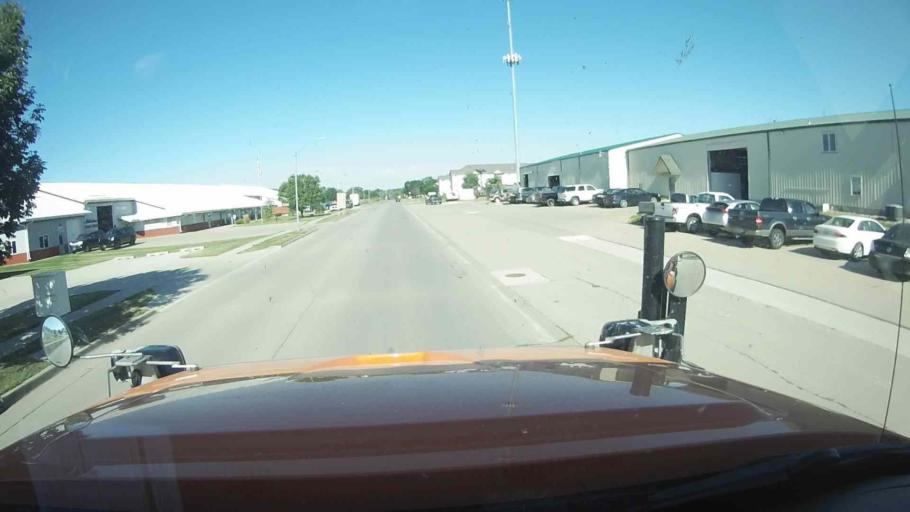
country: US
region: Iowa
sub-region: Polk County
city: Altoona
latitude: 41.6532
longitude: -93.4649
